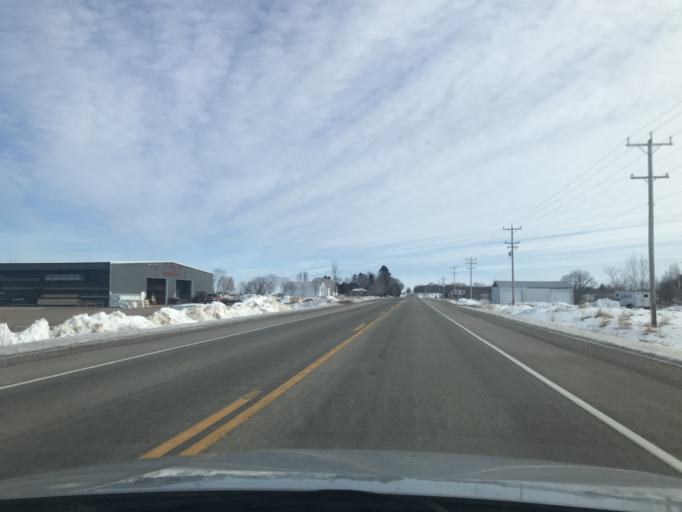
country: US
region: Wisconsin
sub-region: Oconto County
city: Oconto Falls
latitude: 44.8948
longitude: -88.1855
